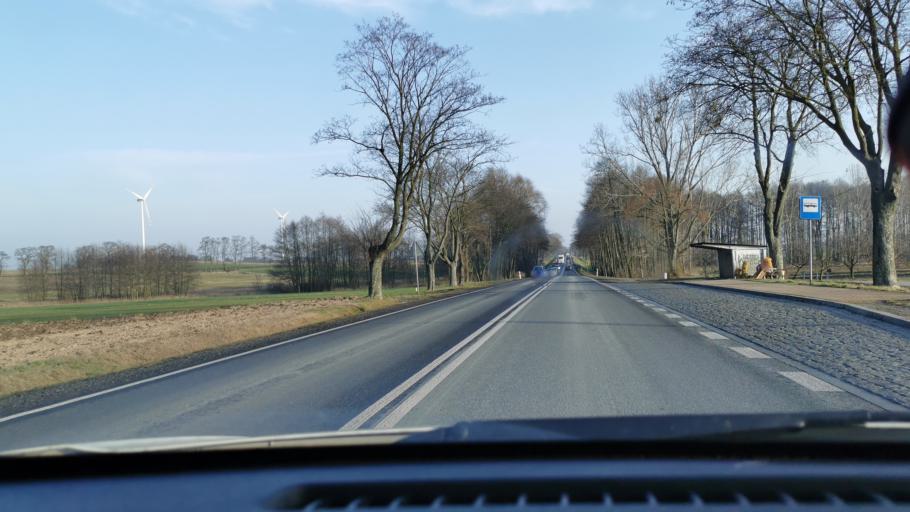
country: PL
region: Lodz Voivodeship
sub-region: Powiat sieradzki
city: Blaszki
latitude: 51.6363
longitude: 18.5249
